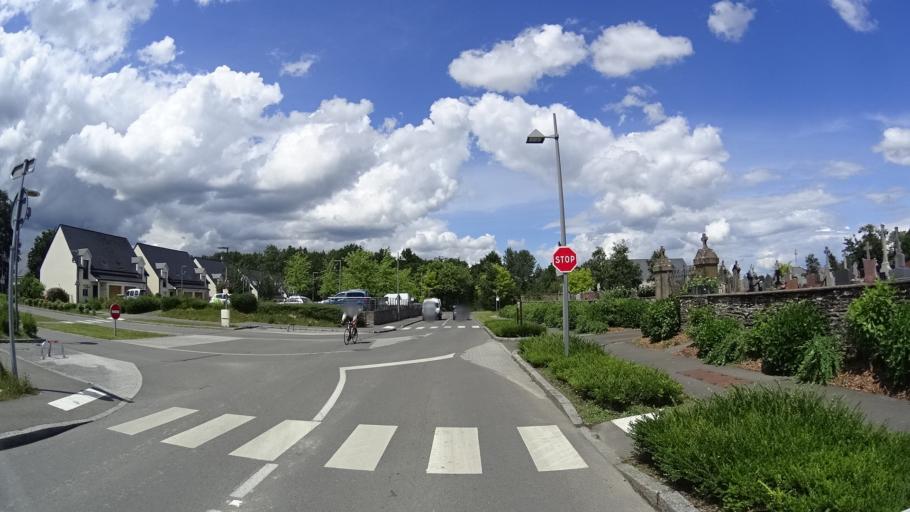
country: FR
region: Brittany
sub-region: Departement d'Ille-et-Vilaine
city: Laille
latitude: 47.9814
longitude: -1.7202
